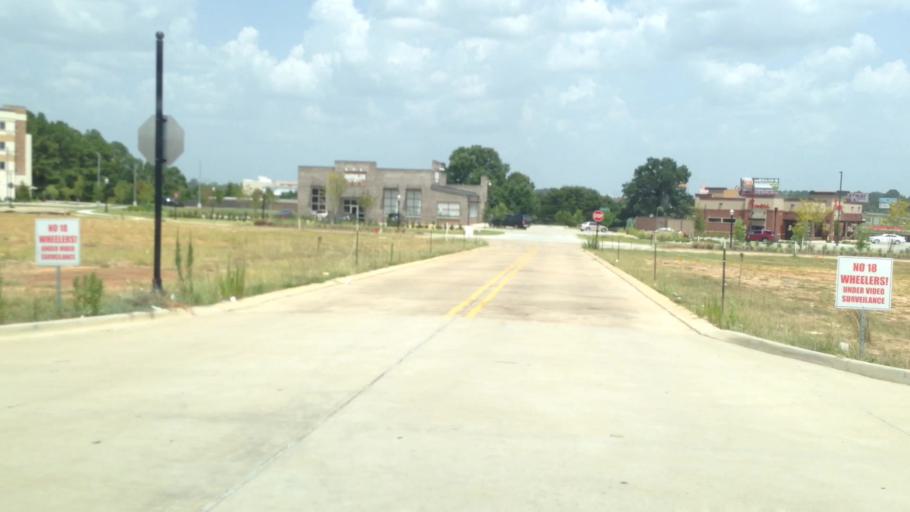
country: US
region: Louisiana
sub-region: Lincoln Parish
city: Ruston
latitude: 32.5416
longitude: -92.6341
